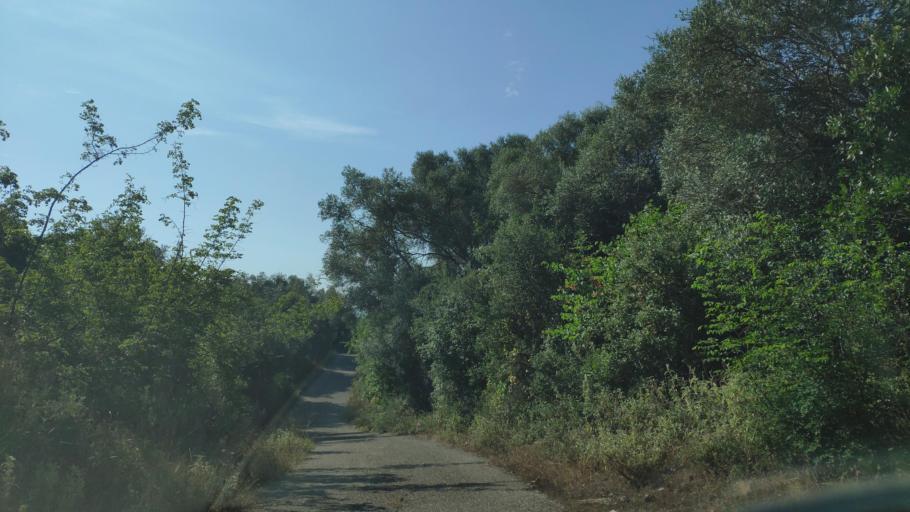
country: GR
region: West Greece
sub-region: Nomos Aitolias kai Akarnanias
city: Fitiai
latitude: 38.6961
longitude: 21.2099
